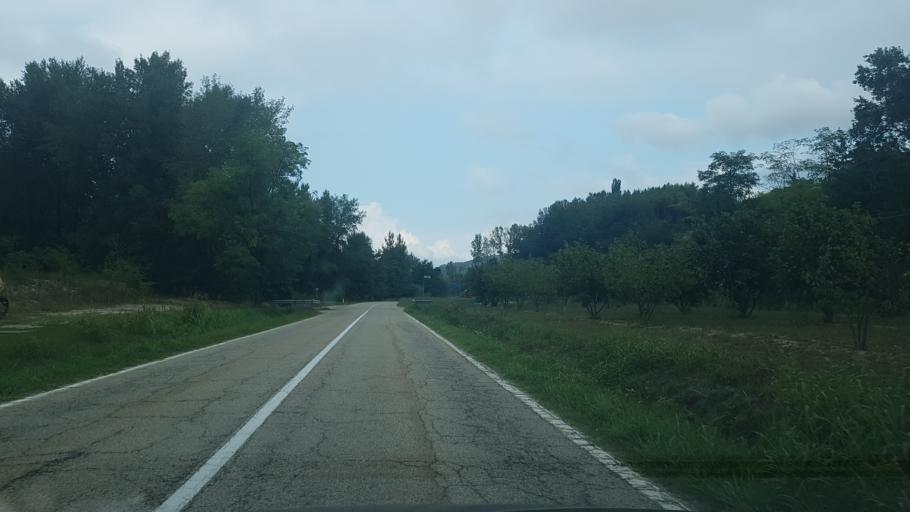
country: IT
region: Piedmont
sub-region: Provincia di Cuneo
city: Cossano Belbo
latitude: 44.6551
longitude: 8.1902
